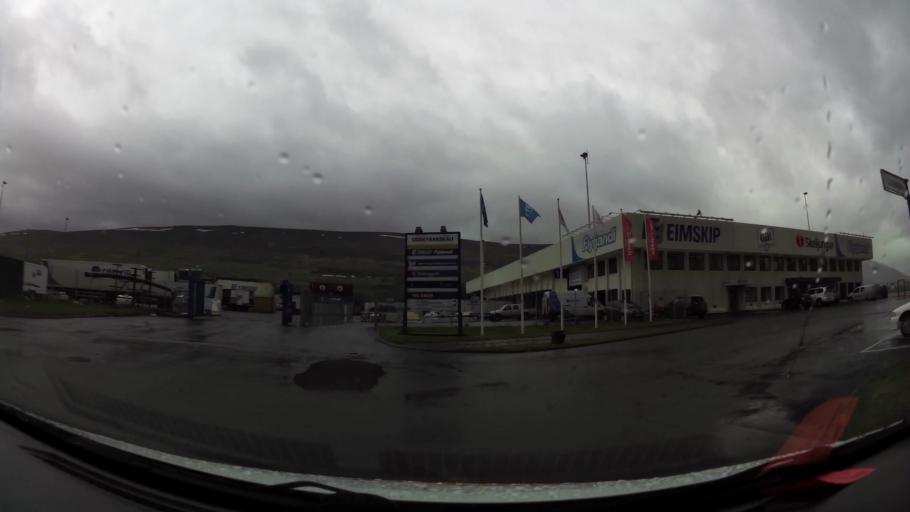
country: IS
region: Northeast
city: Akureyri
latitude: 65.6857
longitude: -18.0791
